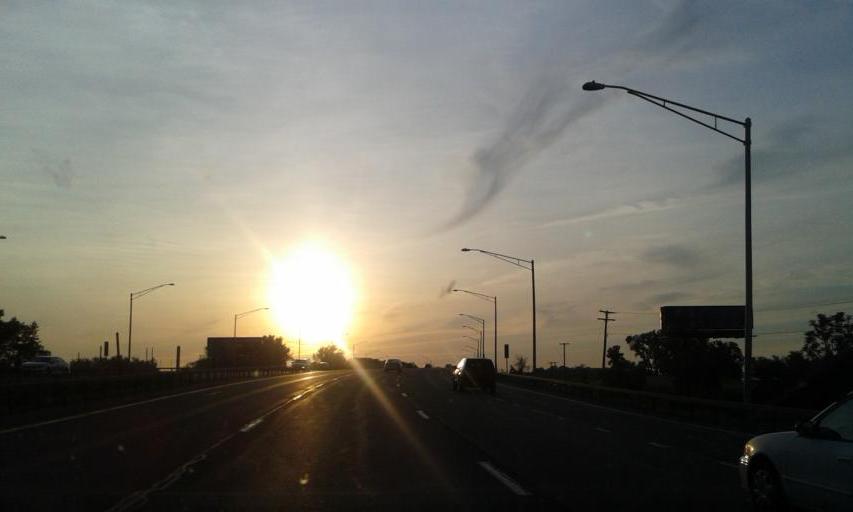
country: US
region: New York
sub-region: Onondaga County
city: Solvay
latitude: 43.0598
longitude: -76.1864
